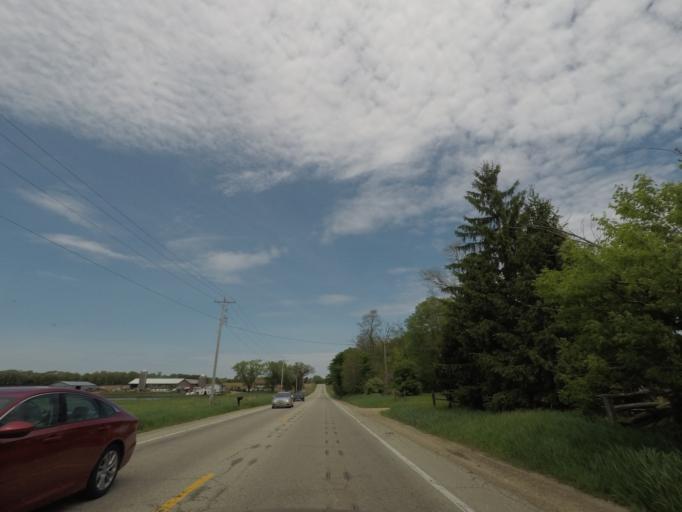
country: US
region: Wisconsin
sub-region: Green County
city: Brooklyn
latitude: 42.8697
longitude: -89.3497
